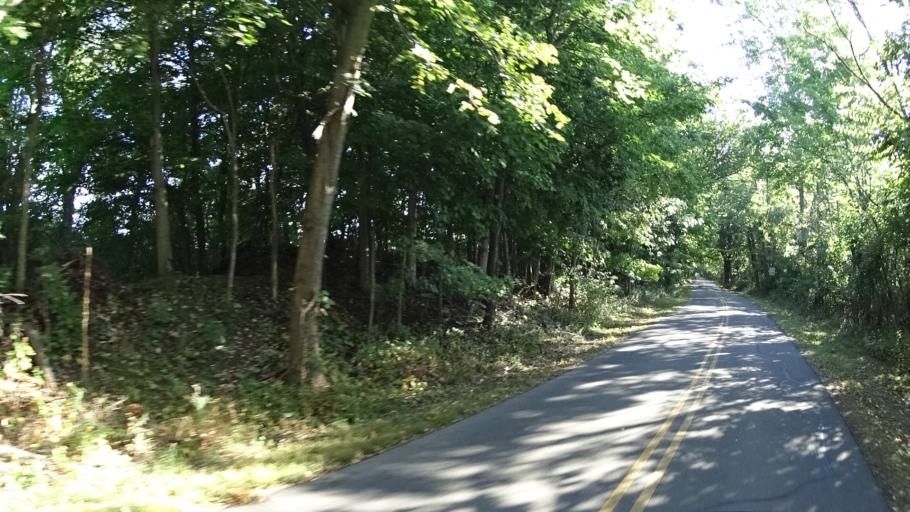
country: US
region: Ohio
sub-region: Erie County
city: Sandusky
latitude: 41.6137
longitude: -82.7137
